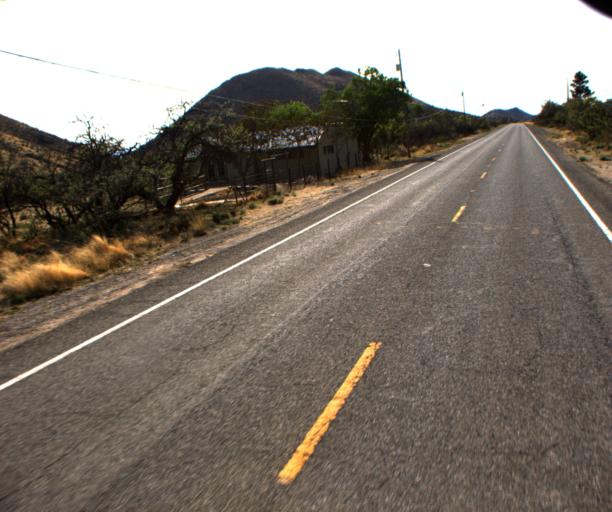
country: US
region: Arizona
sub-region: Cochise County
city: Willcox
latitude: 32.1751
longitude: -109.6140
